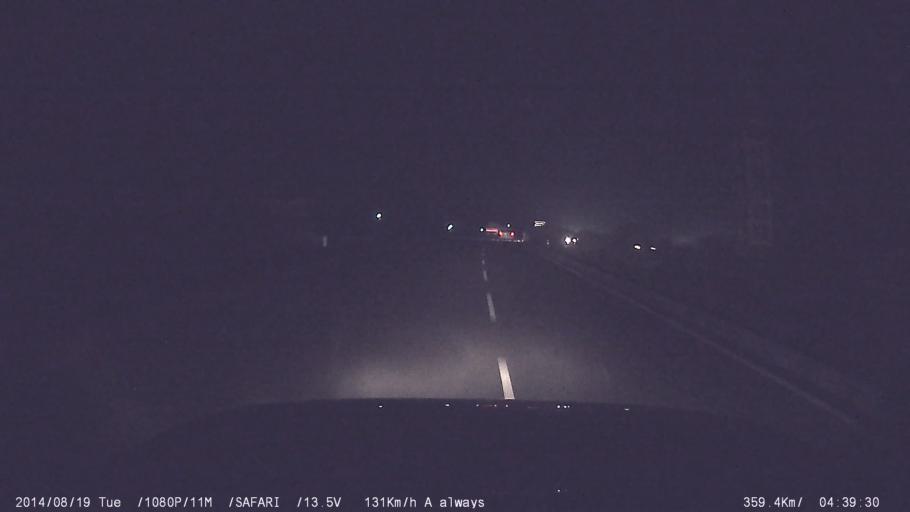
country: IN
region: Tamil Nadu
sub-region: Erode
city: Erode
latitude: 11.3714
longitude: 77.6489
